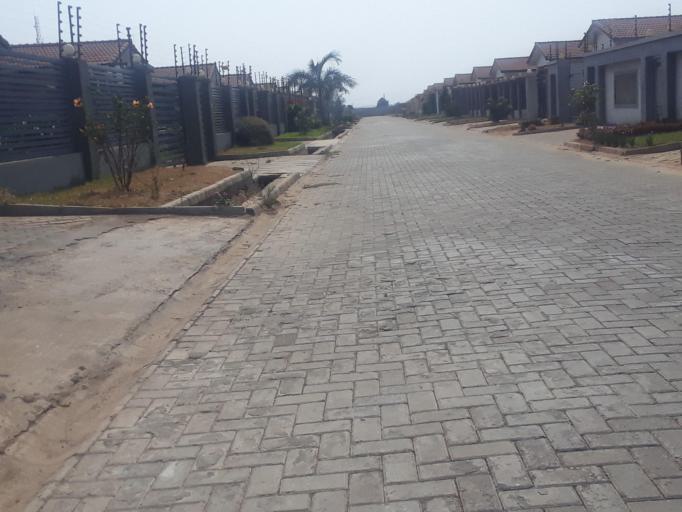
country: ZM
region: Lusaka
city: Lusaka
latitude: -15.3598
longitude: 28.2806
